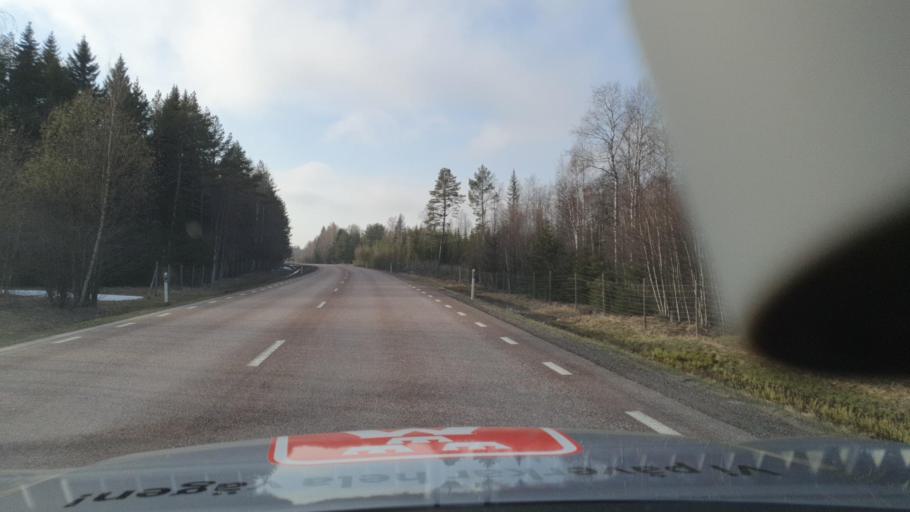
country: SE
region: Vaesterbotten
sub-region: Skelleftea Kommun
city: Burea
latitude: 64.6028
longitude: 21.2017
